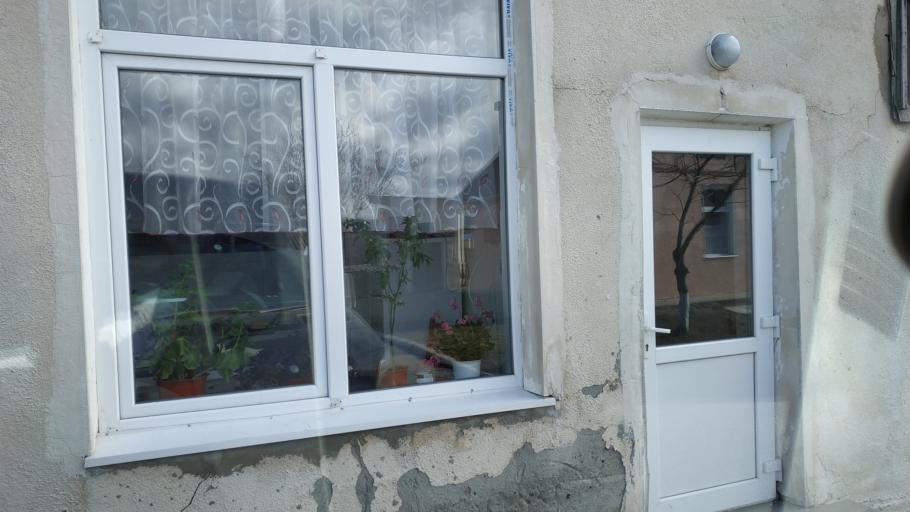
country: MD
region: Stinga Nistrului
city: Bucovat
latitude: 47.1871
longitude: 28.4735
